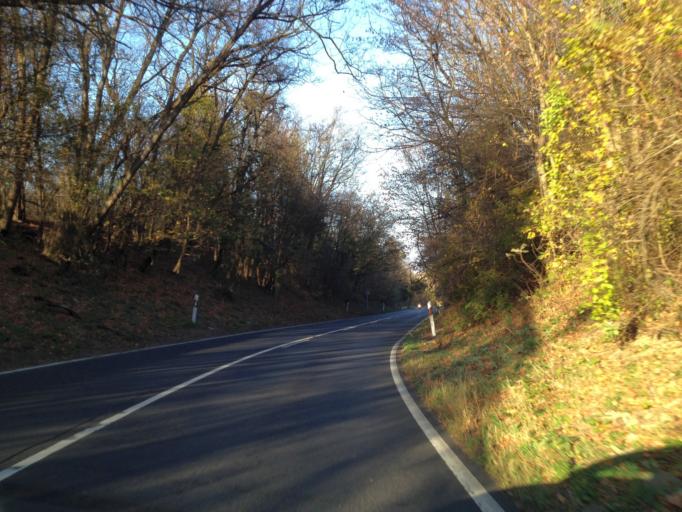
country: HU
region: Veszprem
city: Zirc
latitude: 47.3416
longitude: 17.8782
